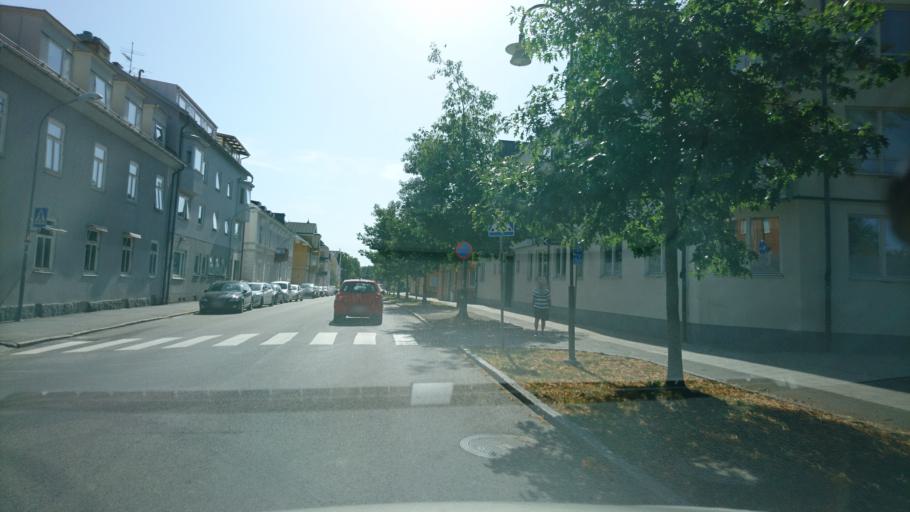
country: SE
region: Soedermanland
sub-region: Strangnas Kommun
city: Strangnas
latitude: 59.3751
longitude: 17.0265
